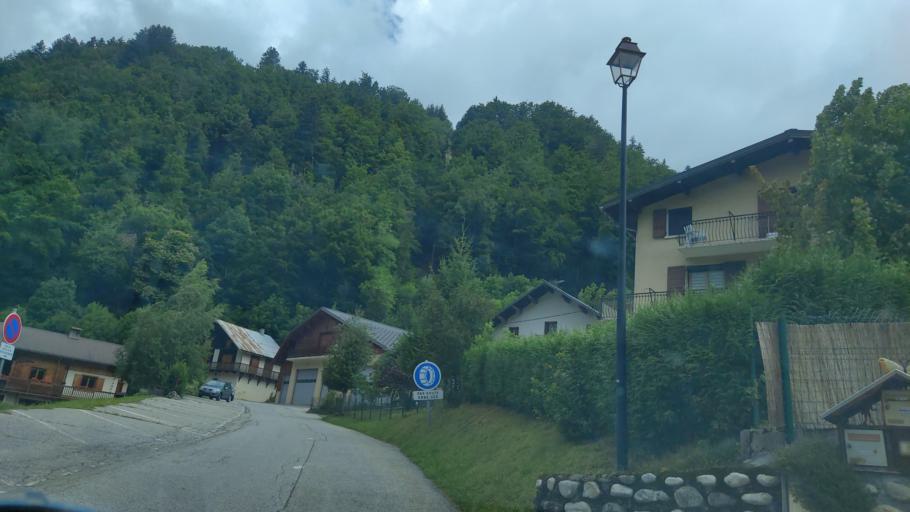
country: FR
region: Rhone-Alpes
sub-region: Departement de la Savoie
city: Beaufort
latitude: 45.7263
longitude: 6.5264
